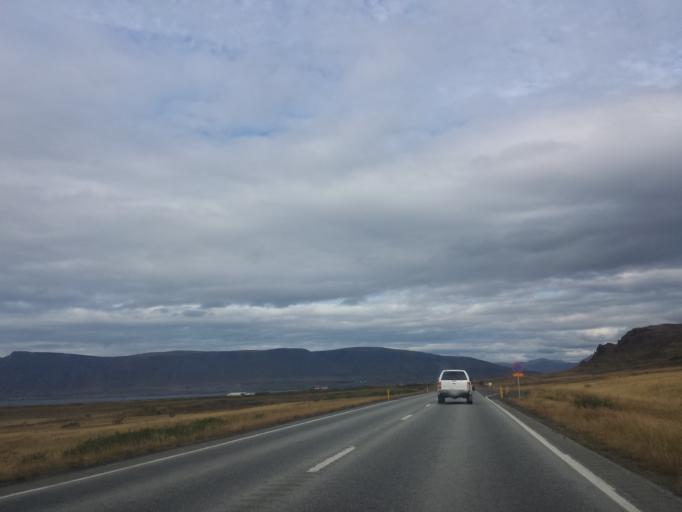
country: IS
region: Capital Region
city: Reykjavik
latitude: 64.2611
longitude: -21.8330
